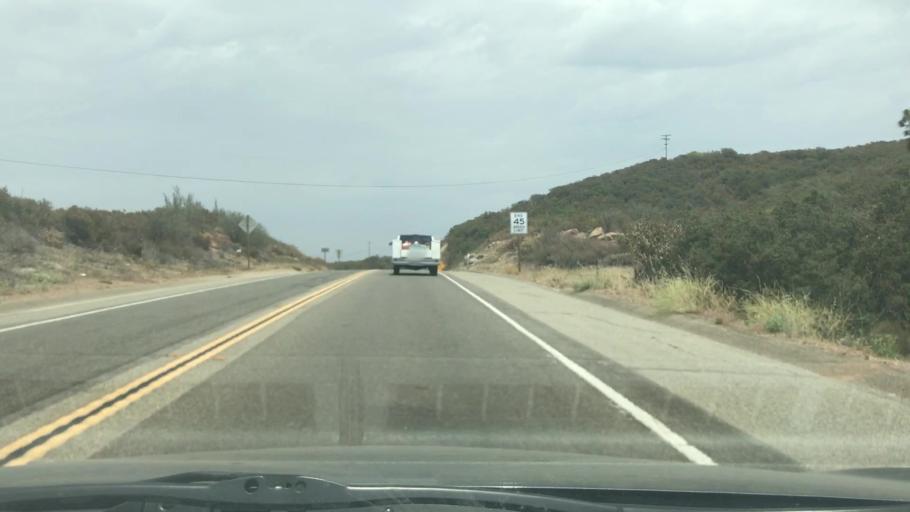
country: US
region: California
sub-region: Riverside County
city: Lakeland Village
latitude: 33.6526
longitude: -117.4061
